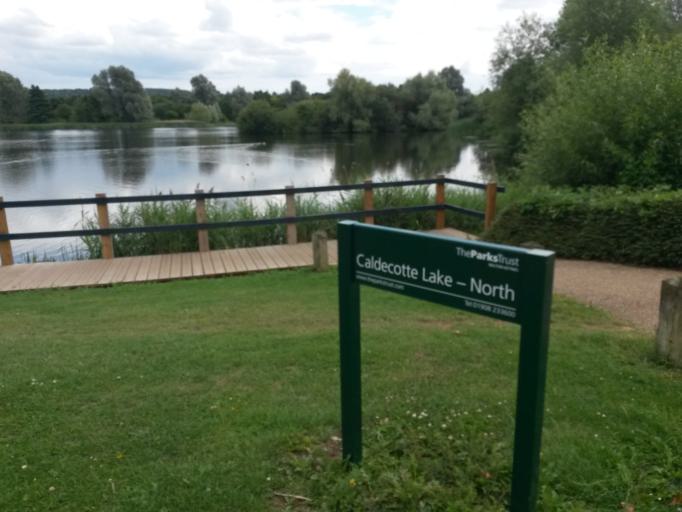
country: GB
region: England
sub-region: Milton Keynes
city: Simpson
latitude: 52.0138
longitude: -0.7030
